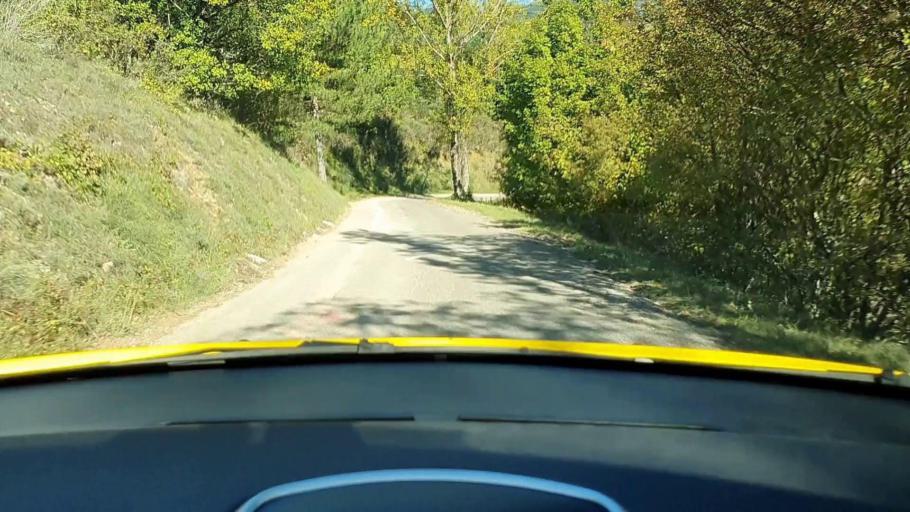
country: FR
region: Languedoc-Roussillon
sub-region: Departement du Gard
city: Aveze
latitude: 43.9606
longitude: 3.4368
